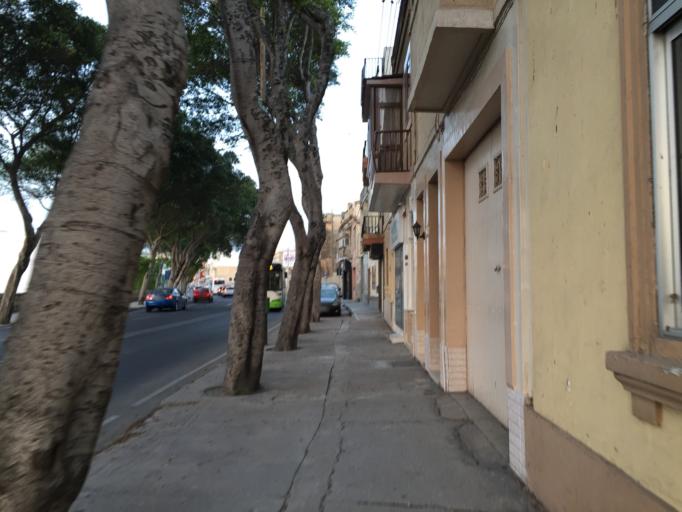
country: MT
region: Haz-Zabbar
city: Zabbar
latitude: 35.8720
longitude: 14.5302
